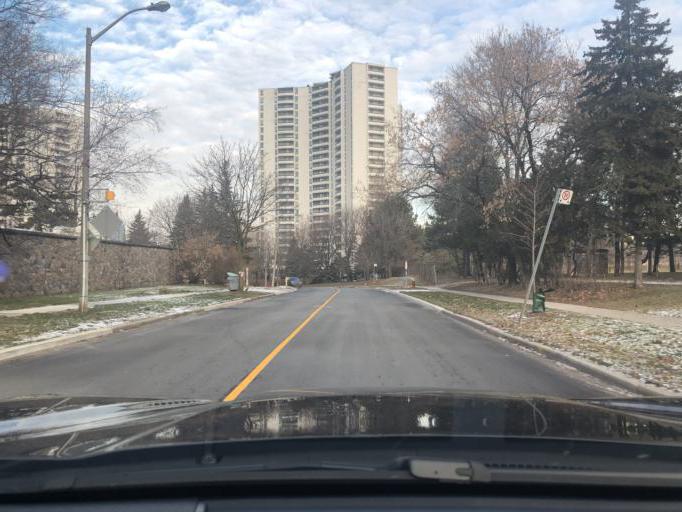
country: CA
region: Ontario
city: Willowdale
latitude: 43.7639
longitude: -79.3420
